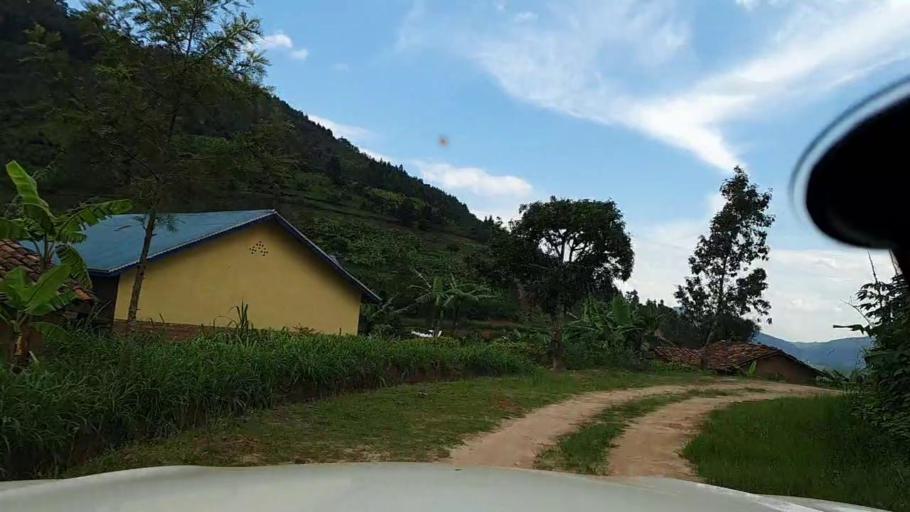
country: RW
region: Southern Province
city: Gitarama
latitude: -1.8025
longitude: 29.7961
